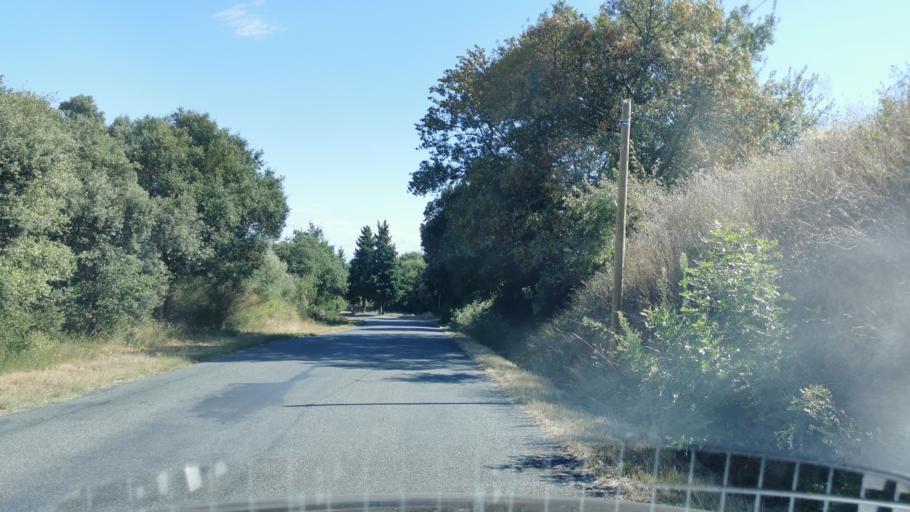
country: FR
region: Languedoc-Roussillon
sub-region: Departement de l'Aude
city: Caunes-Minervois
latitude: 43.3168
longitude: 2.5467
